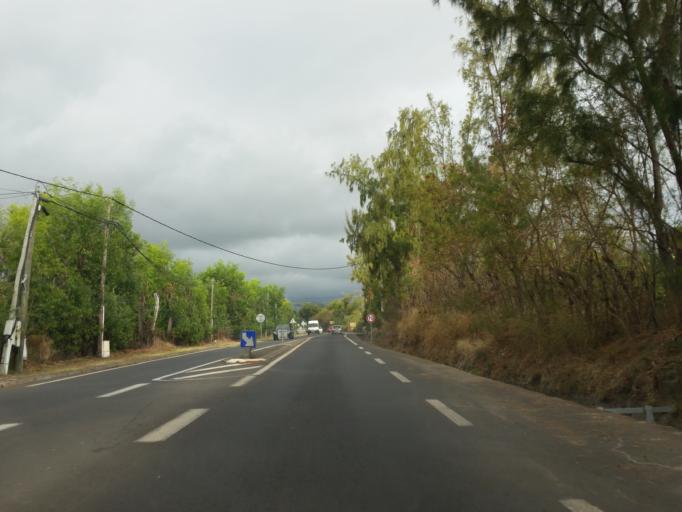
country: RE
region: Reunion
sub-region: Reunion
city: Saint-Paul
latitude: -21.0449
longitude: 55.2300
